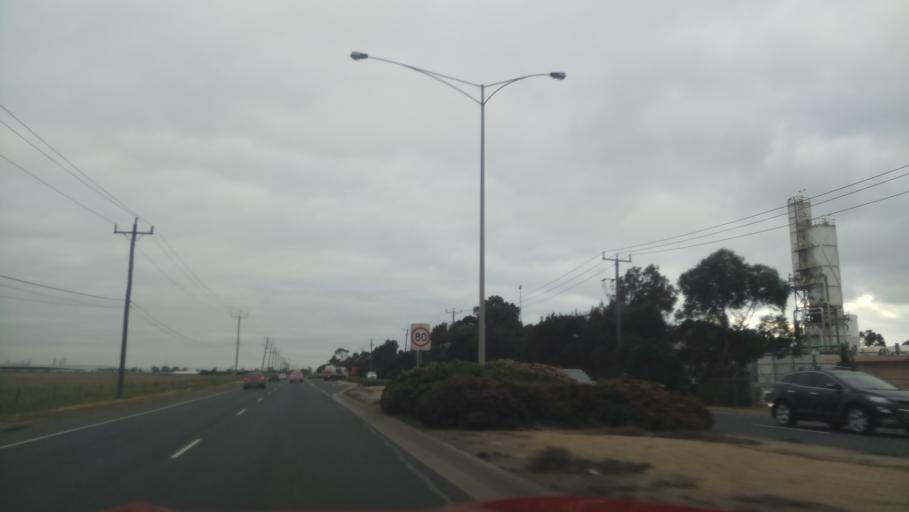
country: AU
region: Victoria
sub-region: Hobsons Bay
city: Laverton
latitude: -37.8450
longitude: 144.7918
